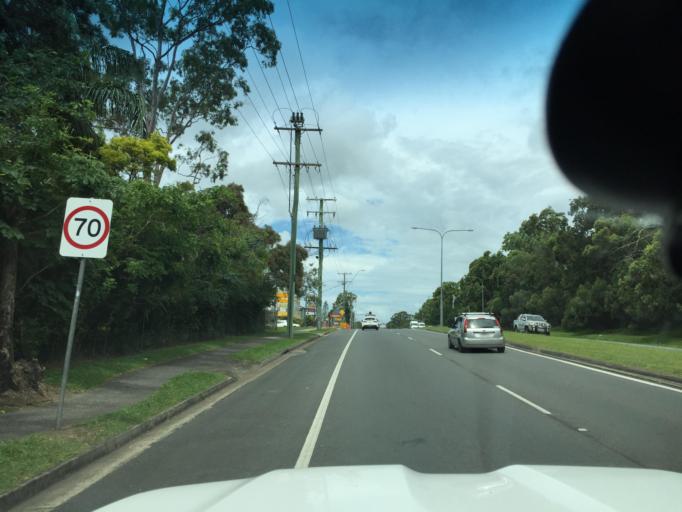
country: AU
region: Queensland
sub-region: Moreton Bay
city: Deception Bay
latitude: -27.1909
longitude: 153.0197
